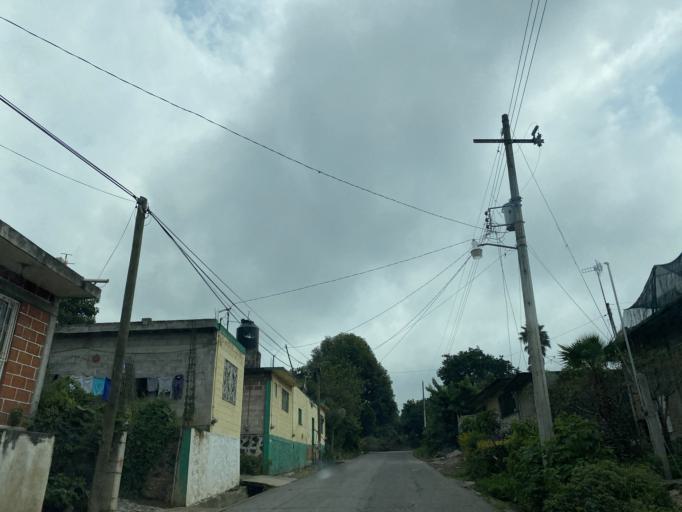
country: MX
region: Morelos
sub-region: Yecapixtla
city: Texcala
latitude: 18.9330
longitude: -98.7996
